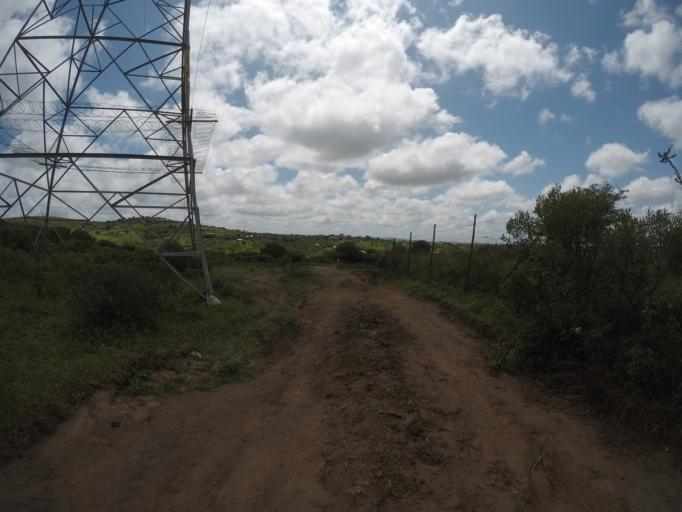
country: ZA
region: KwaZulu-Natal
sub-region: uThungulu District Municipality
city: Empangeni
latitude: -28.5845
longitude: 31.8344
